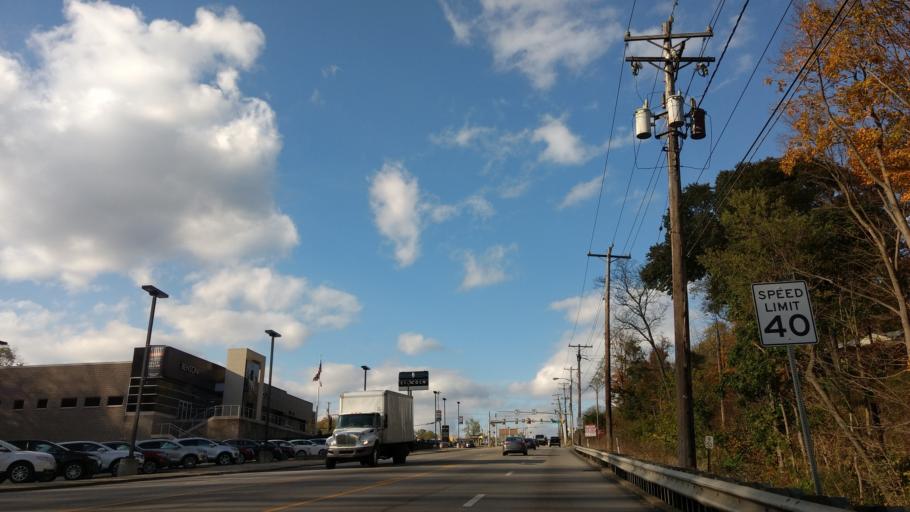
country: US
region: Pennsylvania
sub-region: Allegheny County
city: Baldwin
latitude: 40.3506
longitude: -79.9767
